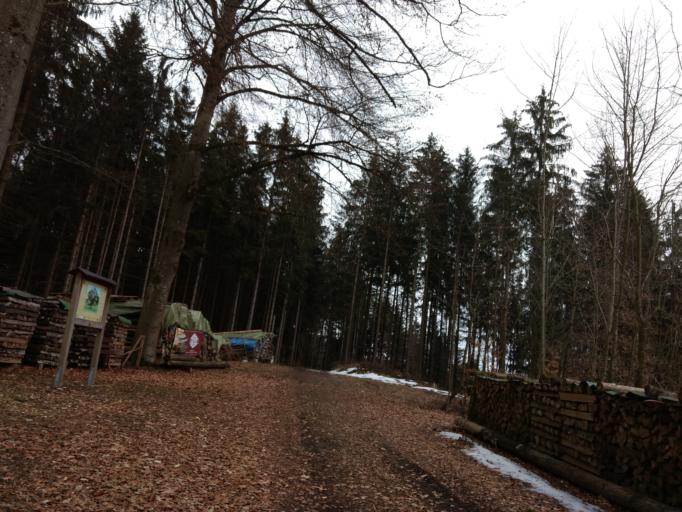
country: AT
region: Upper Austria
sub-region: Politischer Bezirk Rohrbach
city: Atzesberg
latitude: 48.4214
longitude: 13.8793
